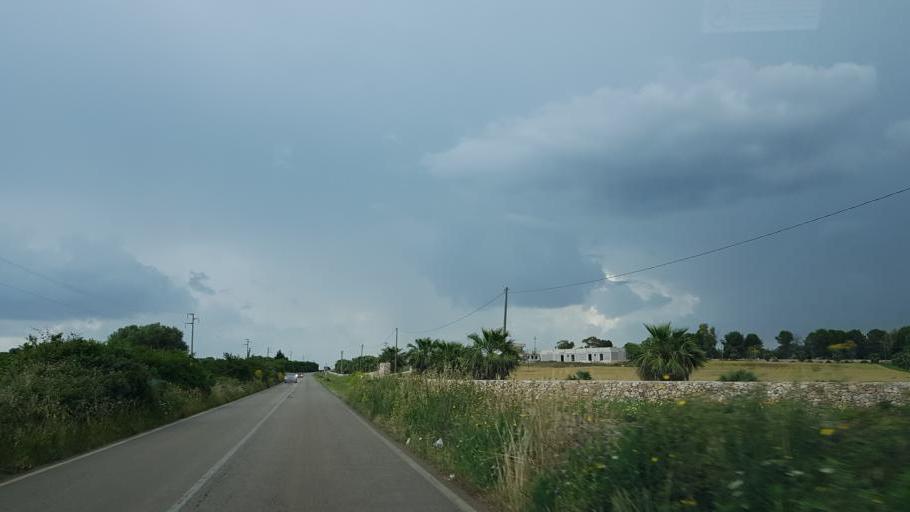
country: IT
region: Apulia
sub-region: Provincia di Lecce
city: Porto Cesareo
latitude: 40.3229
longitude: 17.8558
